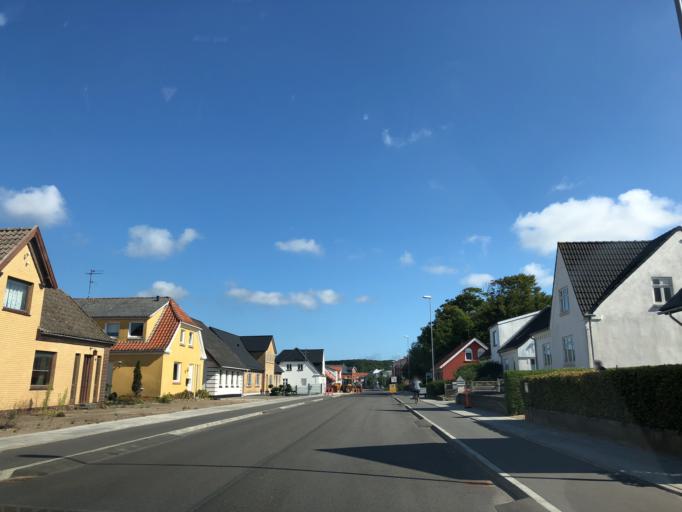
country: DK
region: North Denmark
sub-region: Jammerbugt Kommune
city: Fjerritslev
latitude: 57.0843
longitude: 9.2652
